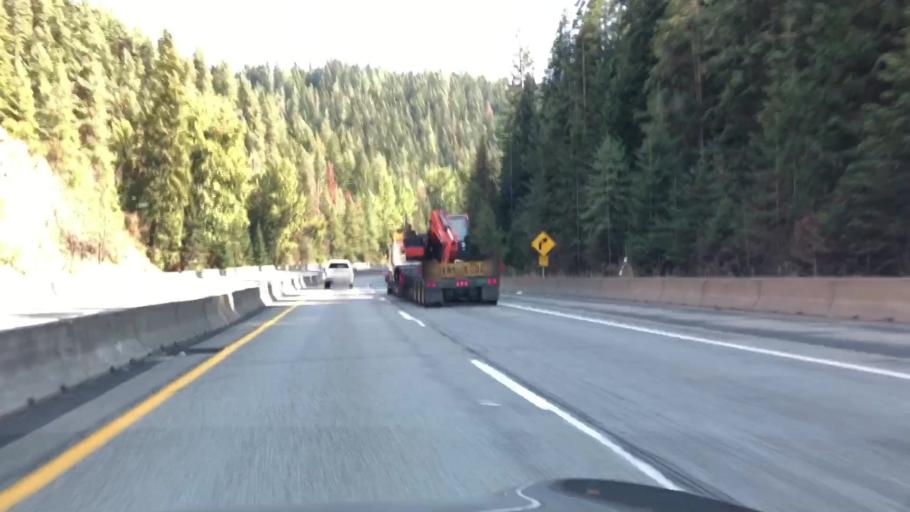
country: US
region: Idaho
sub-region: Shoshone County
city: Pinehurst
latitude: 47.5982
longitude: -116.4958
